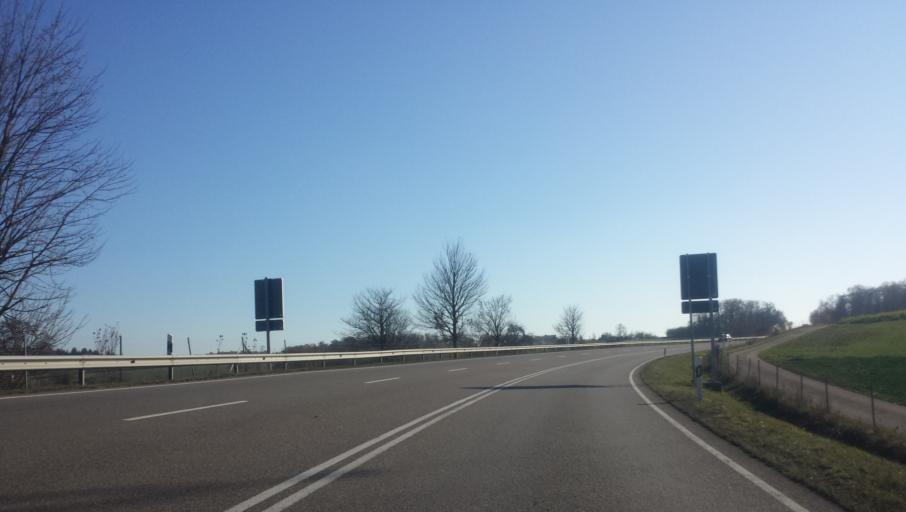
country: DE
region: Baden-Wuerttemberg
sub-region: Karlsruhe Region
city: Binau
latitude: 49.3561
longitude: 9.0369
